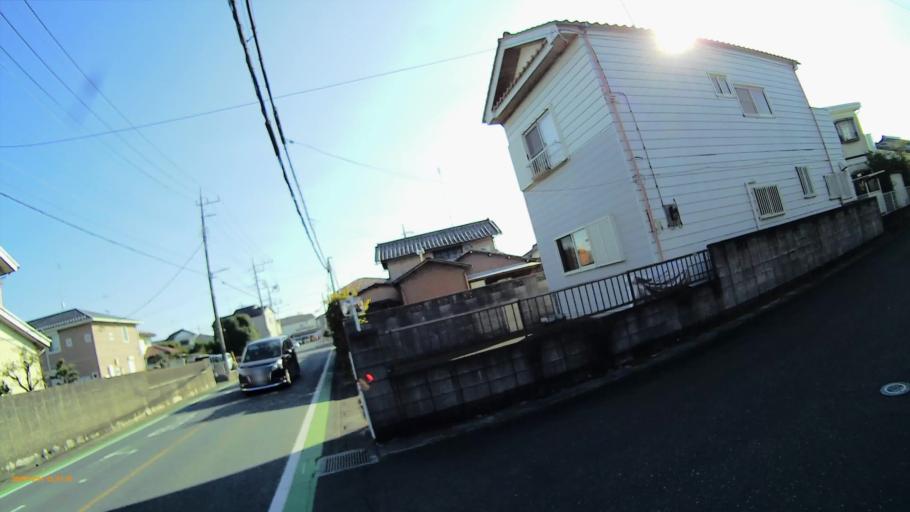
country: JP
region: Saitama
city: Fukiage-fujimi
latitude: 36.0819
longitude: 139.4762
